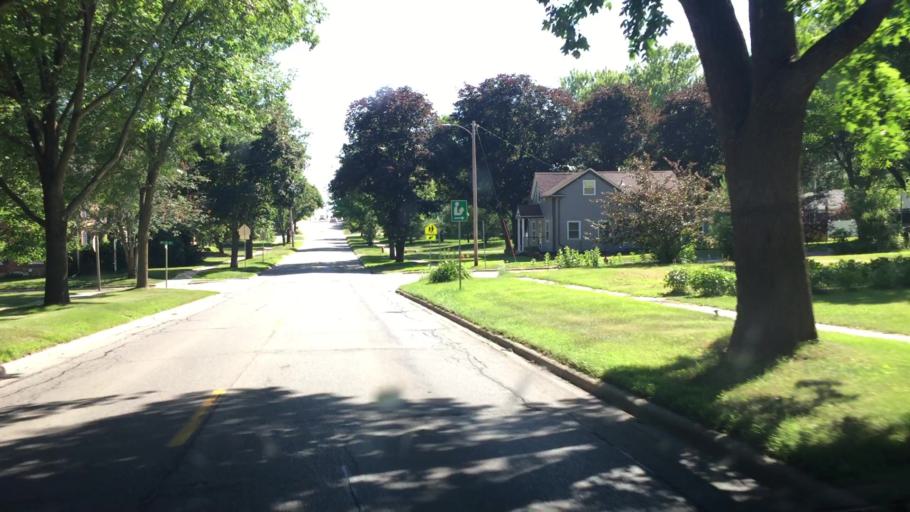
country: US
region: Iowa
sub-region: Linn County
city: Mount Vernon
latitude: 41.9203
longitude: -91.4189
